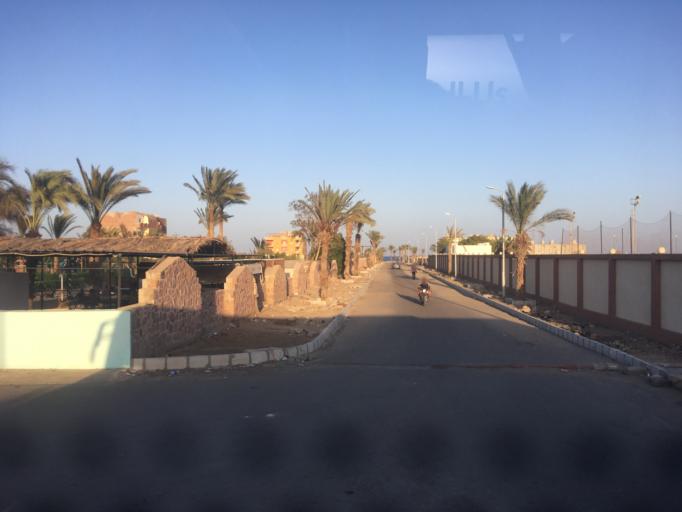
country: EG
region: Red Sea
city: Al Qusayr
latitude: 26.0963
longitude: 34.2793
